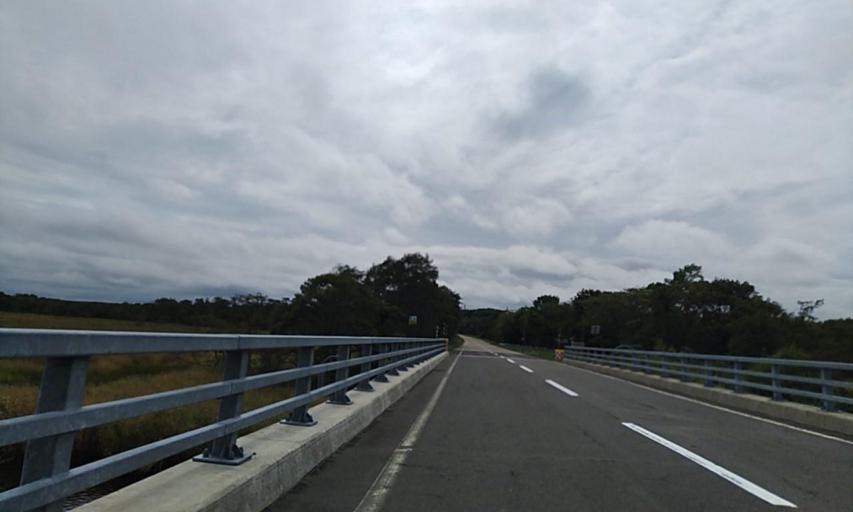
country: JP
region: Hokkaido
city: Shibetsu
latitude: 43.3449
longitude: 145.2148
